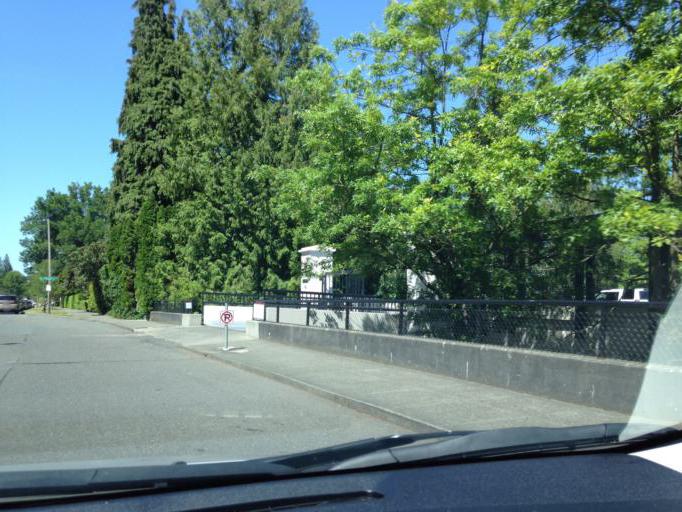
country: US
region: Washington
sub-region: King County
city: Medina
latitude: 47.6280
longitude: -122.2813
